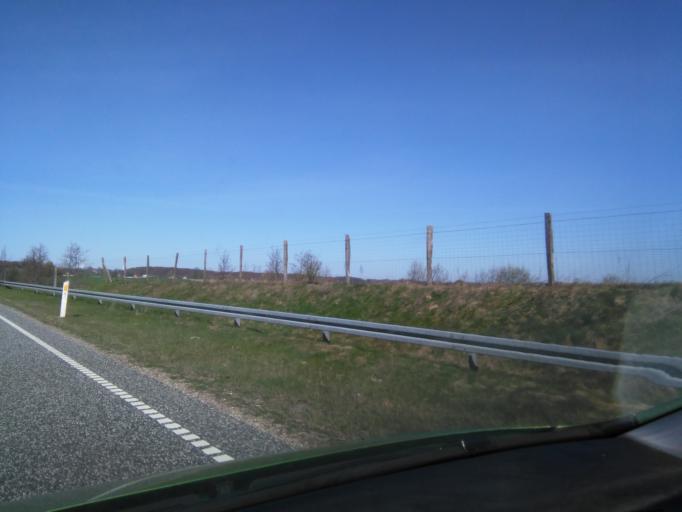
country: DK
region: Central Jutland
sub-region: Hedensted Kommune
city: Hedensted
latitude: 55.8447
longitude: 9.6603
